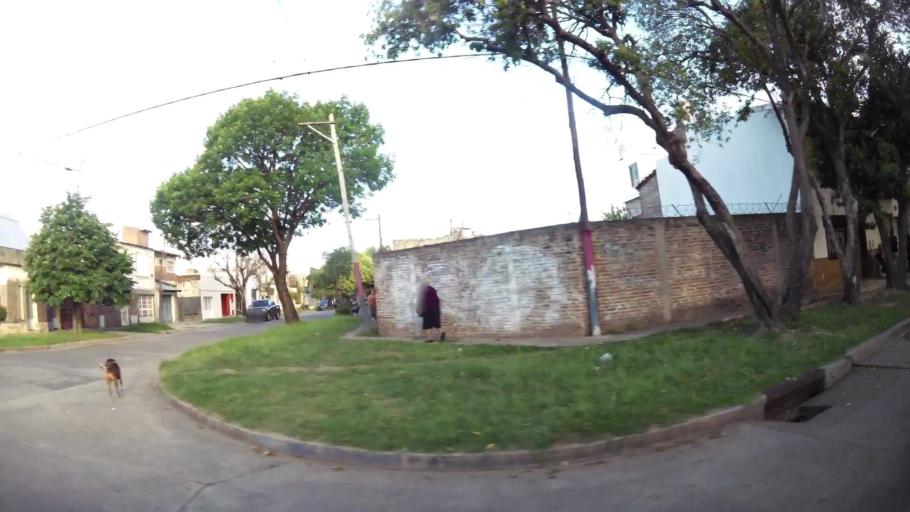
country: AR
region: Santa Fe
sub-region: Departamento de Rosario
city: Rosario
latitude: -32.9774
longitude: -60.6632
